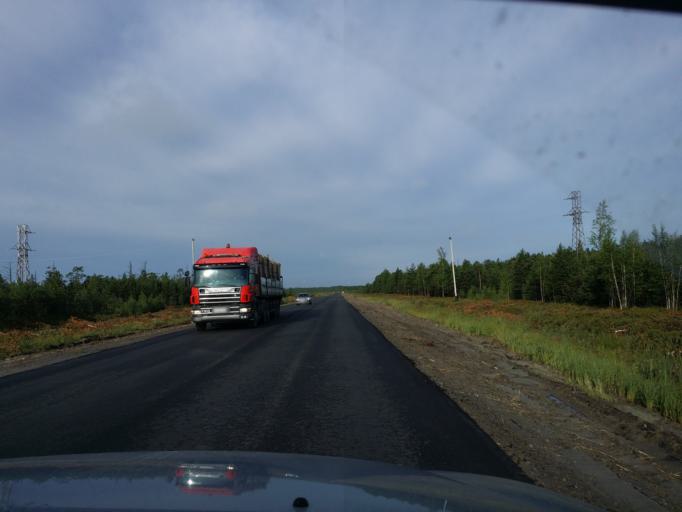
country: RU
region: Tjumen
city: Uvat
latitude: 59.3680
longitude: 69.0068
